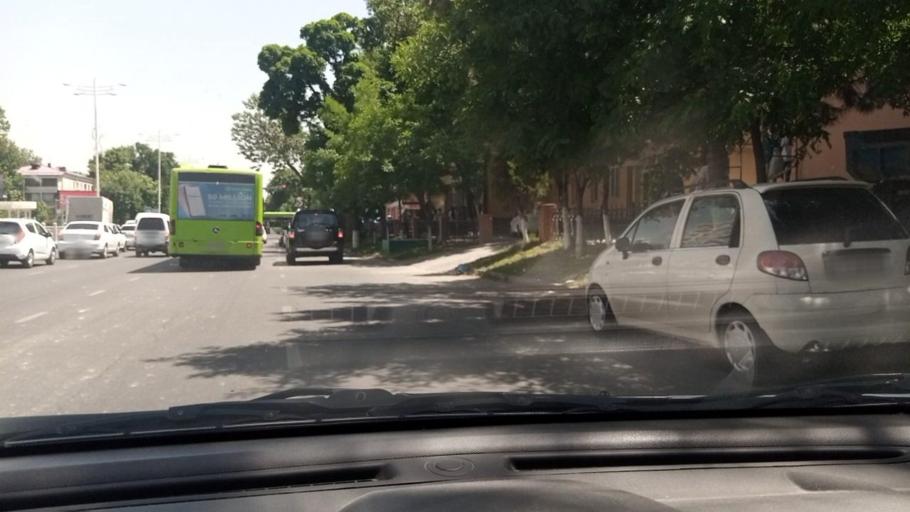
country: UZ
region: Toshkent Shahri
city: Tashkent
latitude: 41.2888
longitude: 69.2282
